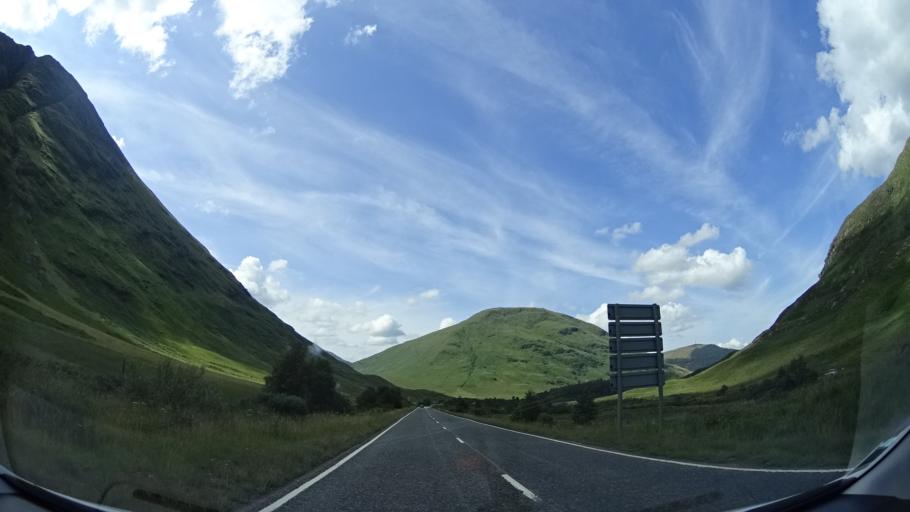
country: GB
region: Scotland
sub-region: Highland
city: Fort William
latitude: 56.6638
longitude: -5.0427
